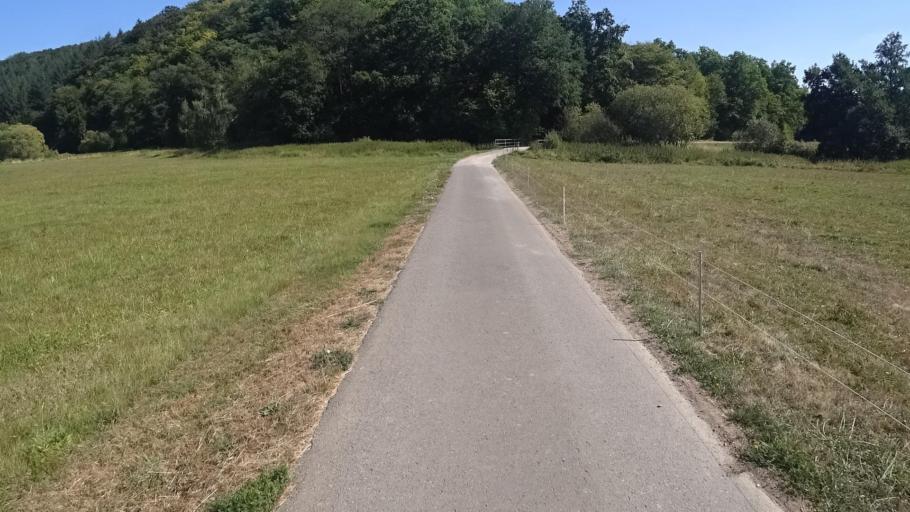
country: DE
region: Rheinland-Pfalz
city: Ravengiersburg
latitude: 49.9298
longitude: 7.4799
